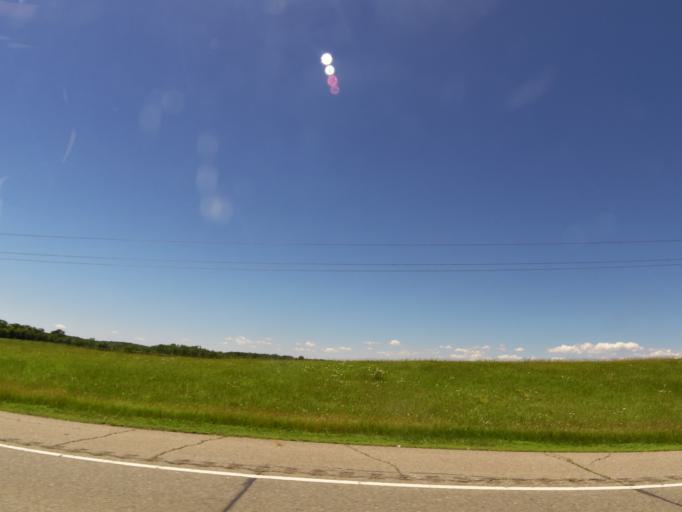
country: US
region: Minnesota
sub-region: Becker County
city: Frazee
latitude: 46.6764
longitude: -95.6693
